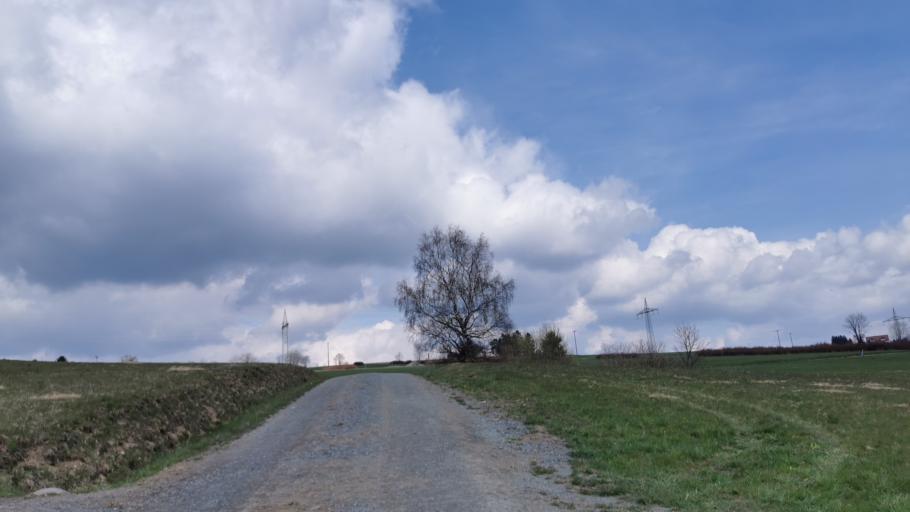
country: DE
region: Bavaria
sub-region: Upper Franconia
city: Teuschnitz
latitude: 50.4313
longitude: 11.3727
